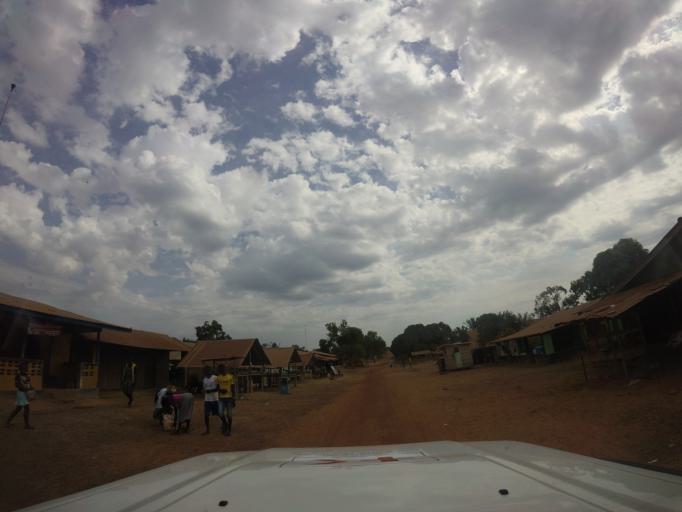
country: LR
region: Grand Cape Mount
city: Robertsport
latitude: 6.9685
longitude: -11.3125
